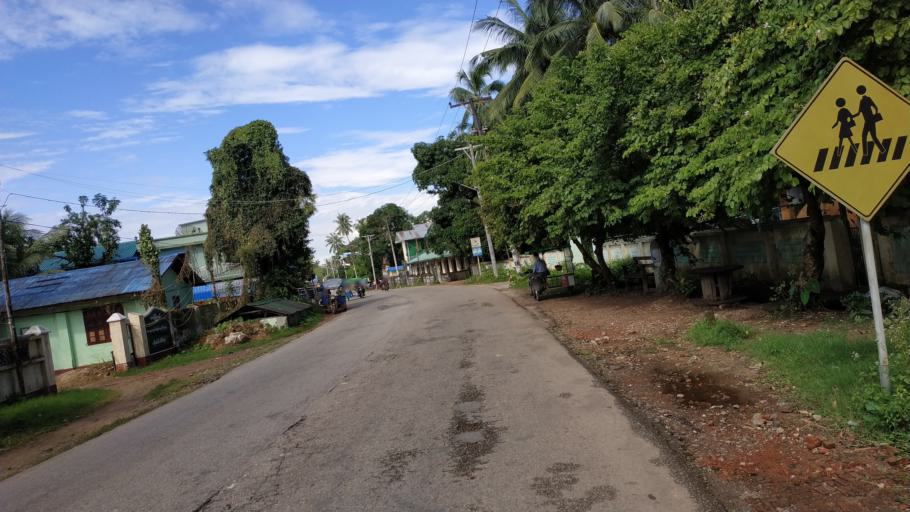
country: MM
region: Mon
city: Thaton
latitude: 16.9137
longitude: 97.3736
